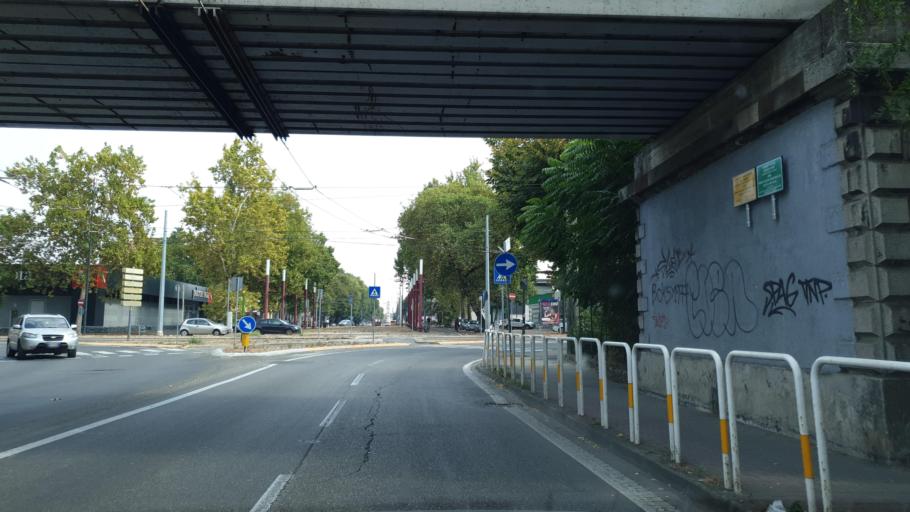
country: IT
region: Emilia-Romagna
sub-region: Provincia di Parma
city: Parma
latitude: 44.8065
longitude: 10.3032
